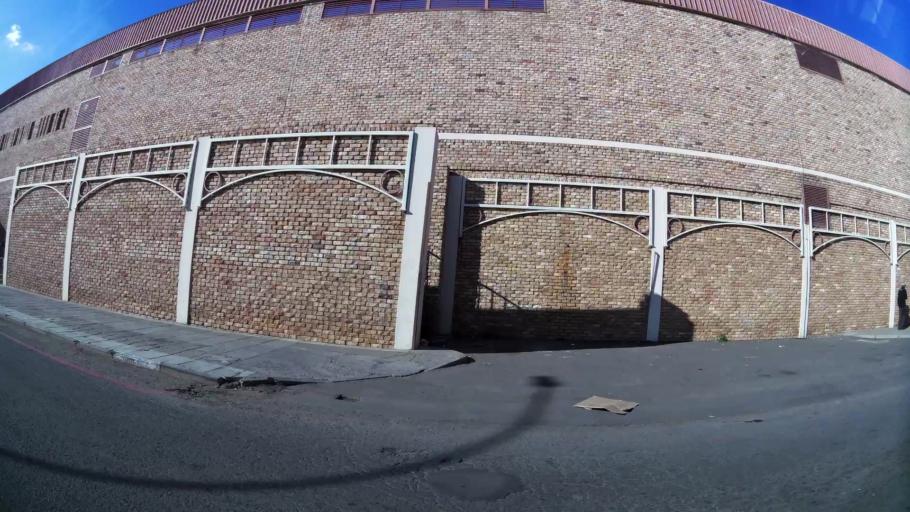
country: ZA
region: Northern Cape
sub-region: Frances Baard District Municipality
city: Kimberley
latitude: -28.7439
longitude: 24.7641
